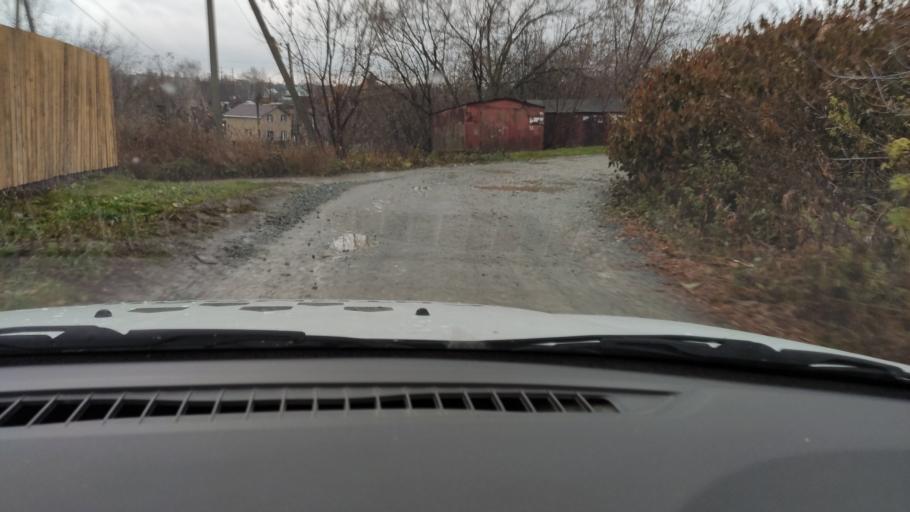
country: RU
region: Perm
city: Sylva
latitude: 58.0443
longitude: 56.7466
